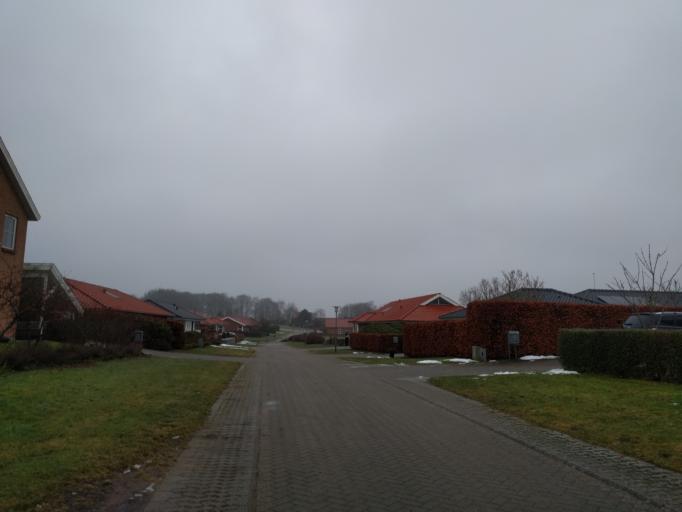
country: DK
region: Central Jutland
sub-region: Viborg Kommune
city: Viborg
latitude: 56.4282
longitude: 9.4074
